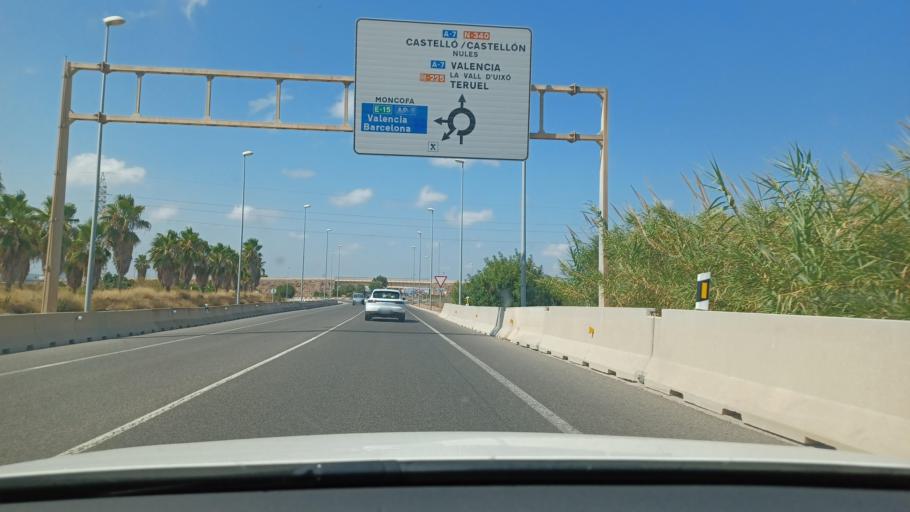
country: ES
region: Valencia
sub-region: Provincia de Castello
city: Moncofar
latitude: 39.8136
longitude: -0.1673
